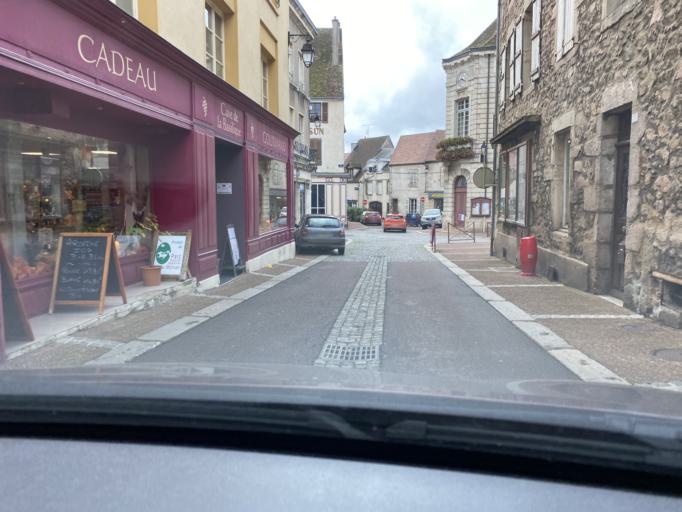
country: FR
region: Bourgogne
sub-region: Departement de la Cote-d'Or
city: Saulieu
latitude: 47.2795
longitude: 4.2293
